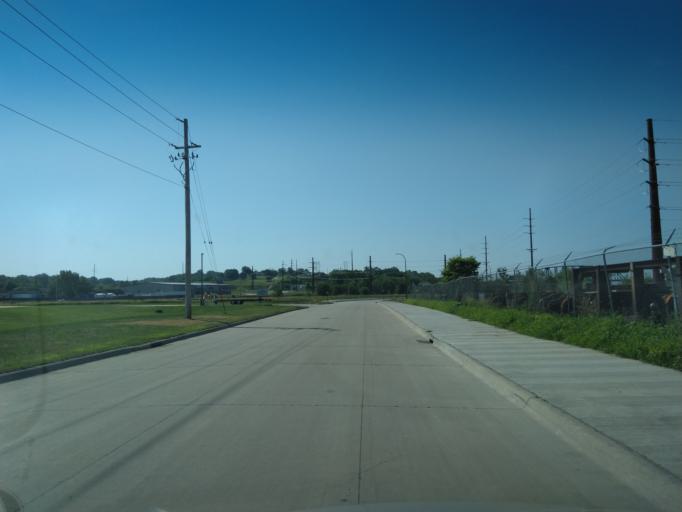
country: US
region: Iowa
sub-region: Woodbury County
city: Sioux City
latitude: 42.4815
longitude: -96.3860
